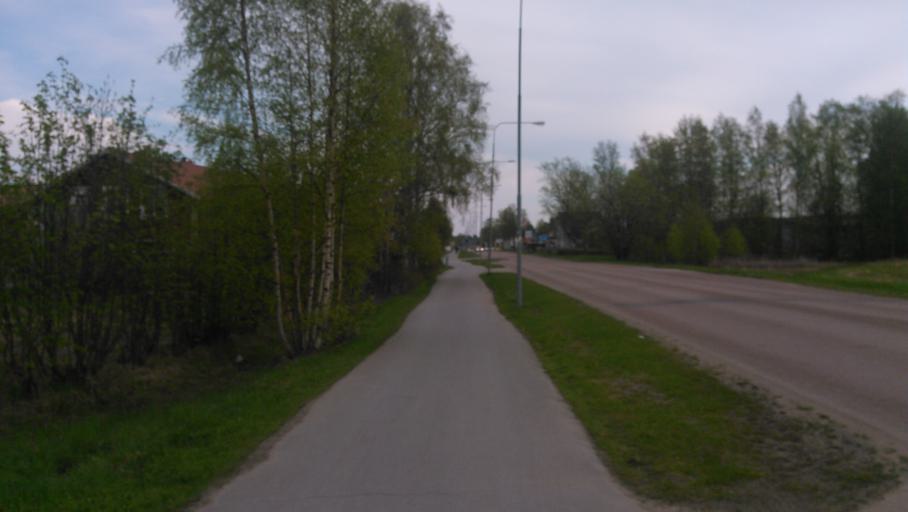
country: SE
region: Vaesterbotten
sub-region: Umea Kommun
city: Umea
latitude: 63.8086
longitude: 20.2714
